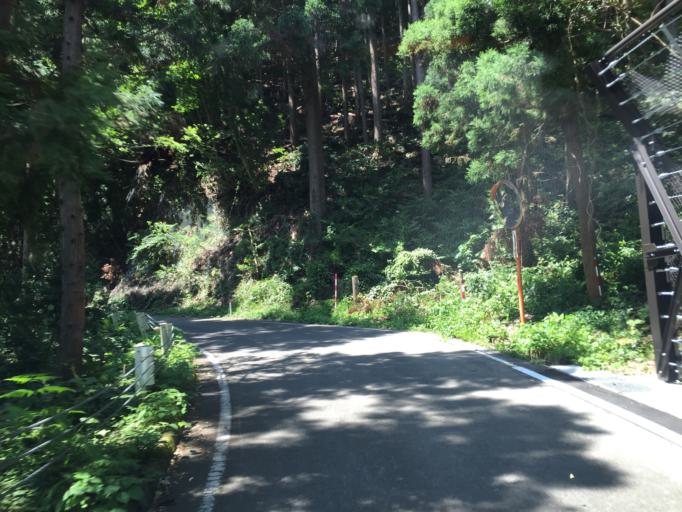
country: JP
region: Fukushima
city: Inawashiro
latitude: 37.4680
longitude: 140.0441
